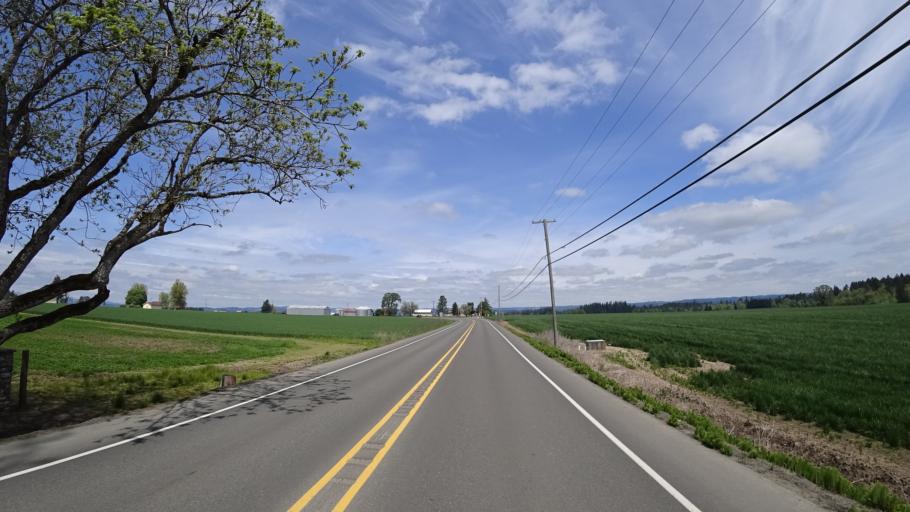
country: US
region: Oregon
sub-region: Washington County
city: North Plains
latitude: 45.5598
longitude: -122.9994
